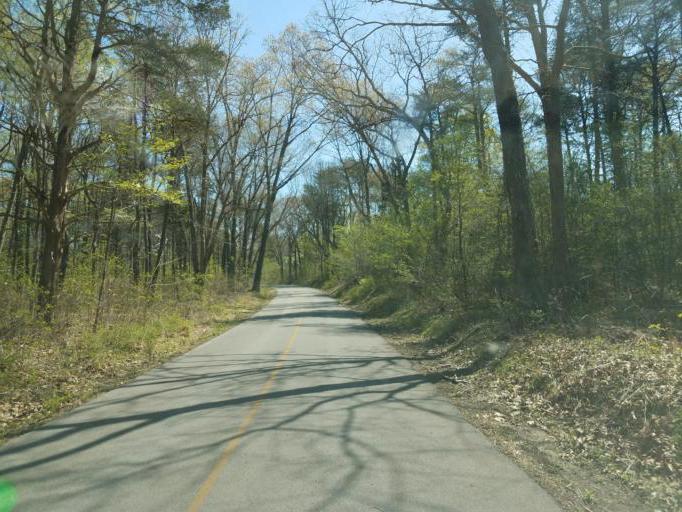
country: US
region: Kentucky
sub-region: Barren County
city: Cave City
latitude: 37.1957
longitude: -86.0589
